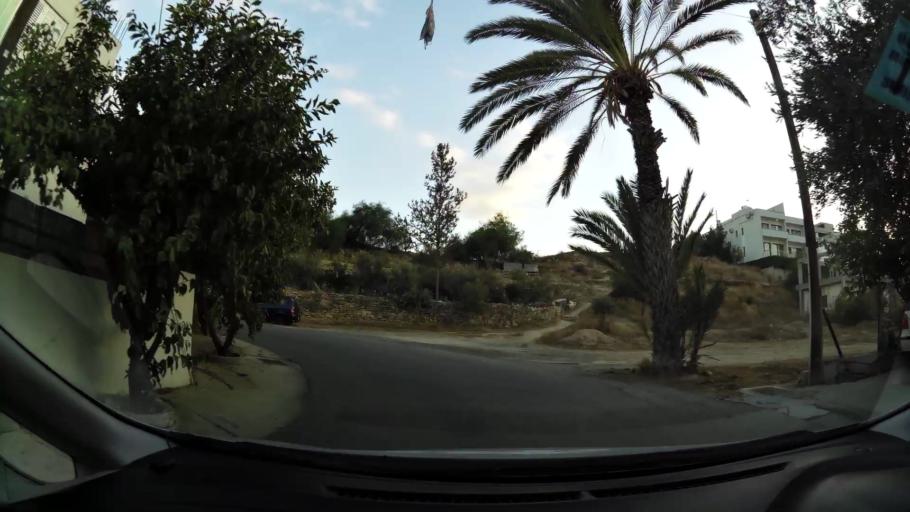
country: CY
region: Lefkosia
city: Nicosia
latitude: 35.1547
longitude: 33.3918
